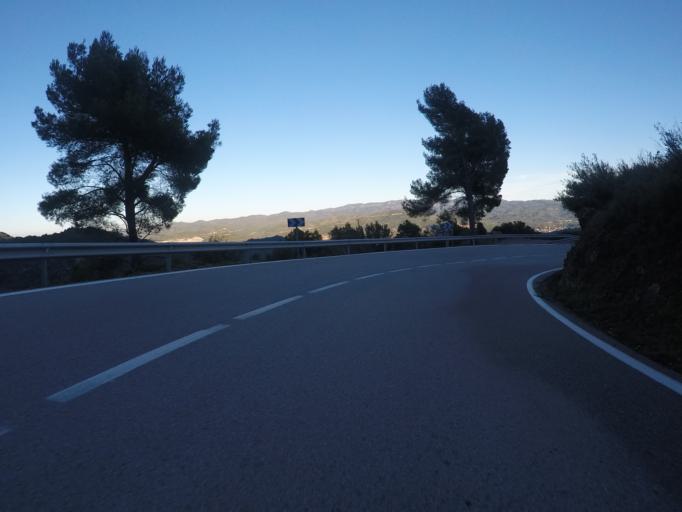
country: ES
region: Catalonia
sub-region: Provincia de Barcelona
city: Monistrol de Montserrat
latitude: 41.6161
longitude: 1.8376
